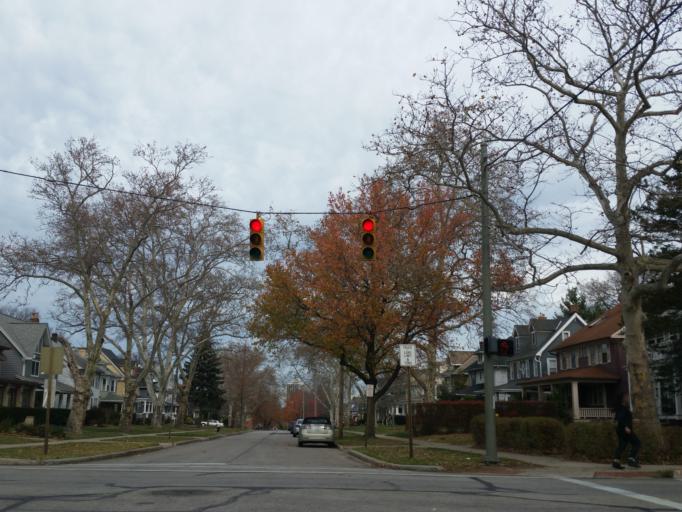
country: US
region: Ohio
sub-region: Cuyahoga County
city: Lakewood
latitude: 41.4804
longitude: -81.7790
